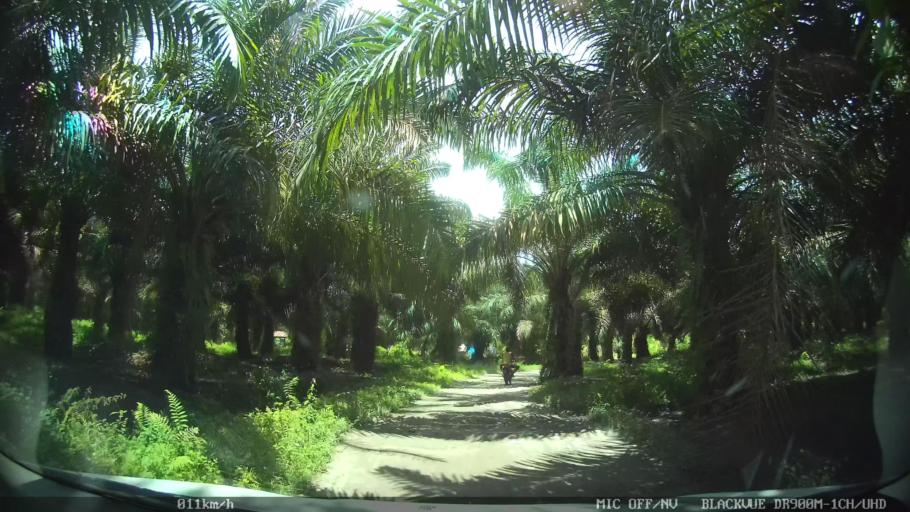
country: ID
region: North Sumatra
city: Percut
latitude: 3.5389
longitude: 98.8707
